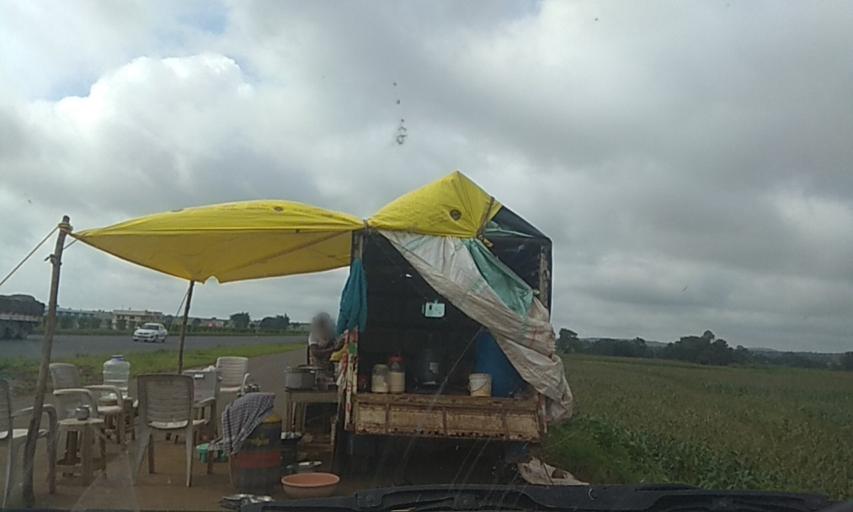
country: IN
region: Karnataka
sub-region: Haveri
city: Shiggaon
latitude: 15.0959
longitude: 75.1524
